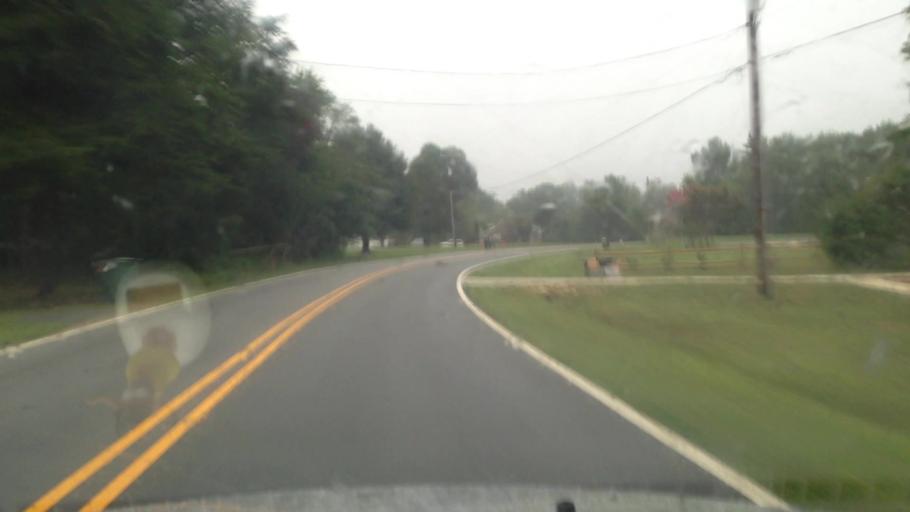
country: US
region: North Carolina
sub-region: Forsyth County
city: Walkertown
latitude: 36.1565
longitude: -80.1239
